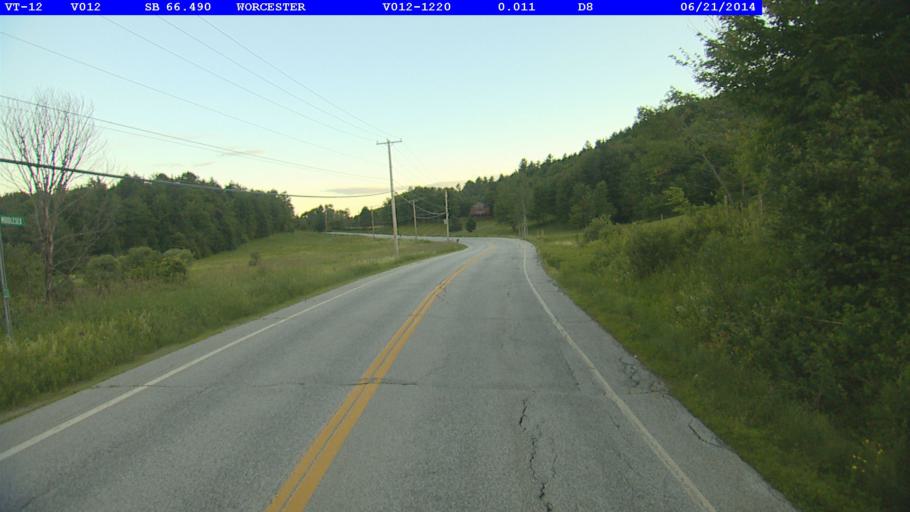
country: US
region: Vermont
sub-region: Washington County
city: Montpelier
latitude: 44.3529
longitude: -72.5650
